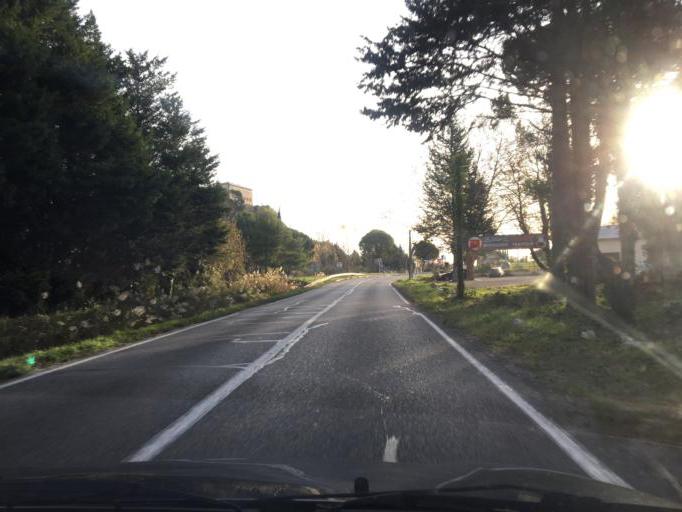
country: FR
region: Provence-Alpes-Cote d'Azur
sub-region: Departement du Vaucluse
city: Lauris
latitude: 43.7462
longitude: 5.3055
